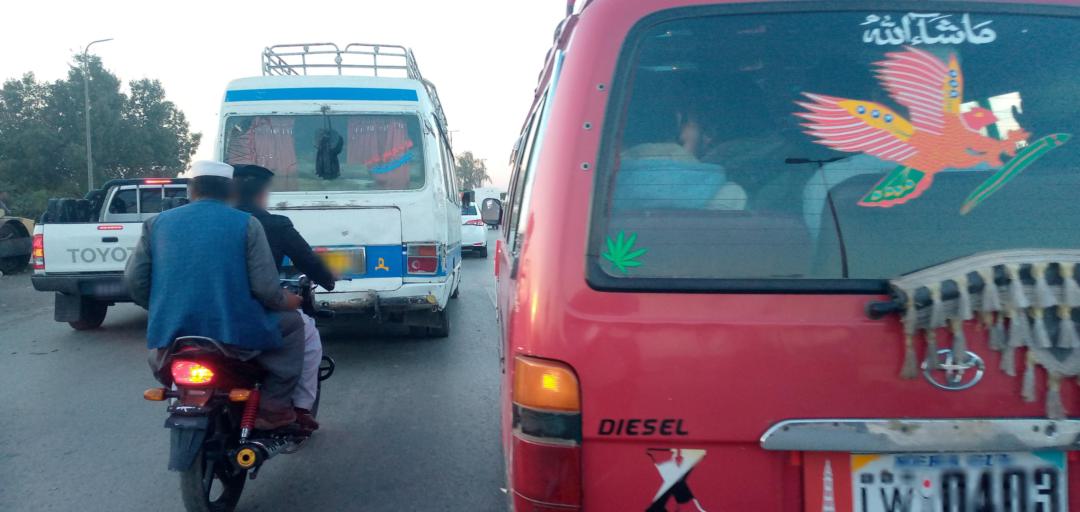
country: PK
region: Khyber Pakhtunkhwa
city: Peshawar
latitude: 34.0259
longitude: 71.6189
